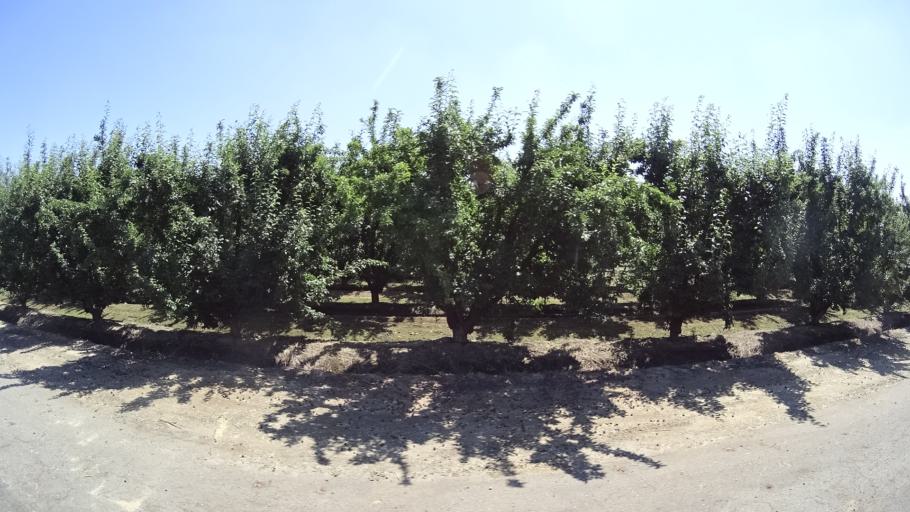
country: US
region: California
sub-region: Fresno County
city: Kingsburg
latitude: 36.4458
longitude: -119.6005
